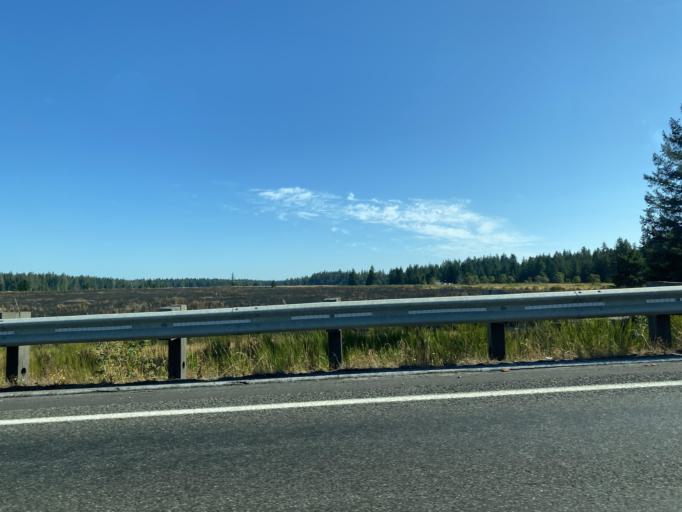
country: US
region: Washington
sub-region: Thurston County
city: Rainier
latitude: 46.9036
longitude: -122.7245
